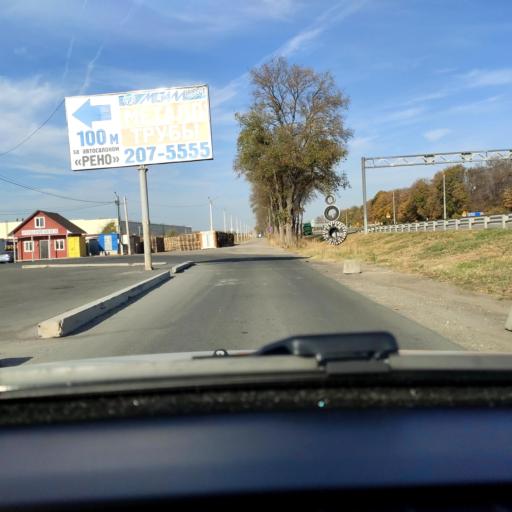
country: RU
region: Voronezj
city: Podgornoye
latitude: 51.8022
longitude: 39.2027
